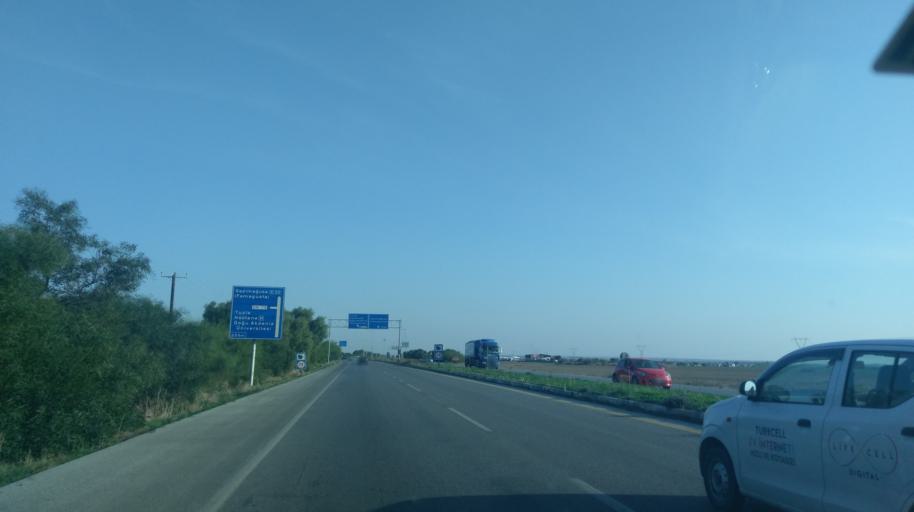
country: CY
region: Ammochostos
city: Acheritou
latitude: 35.1553
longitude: 33.8429
